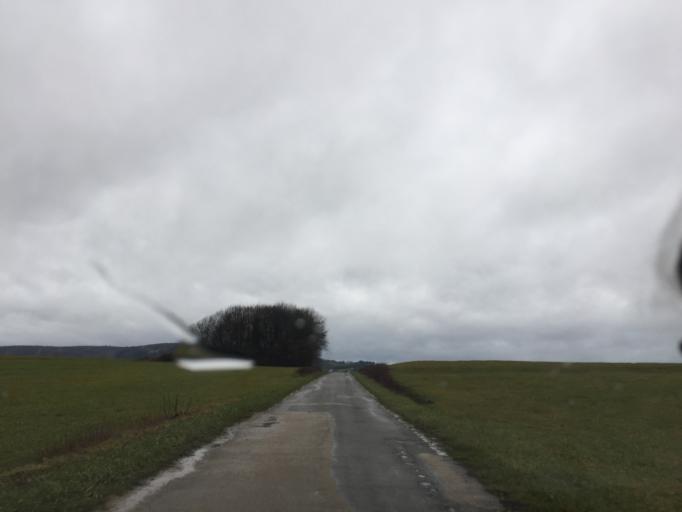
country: FR
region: Franche-Comte
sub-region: Departement du Jura
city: Orchamps
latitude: 47.1969
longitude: 5.6449
